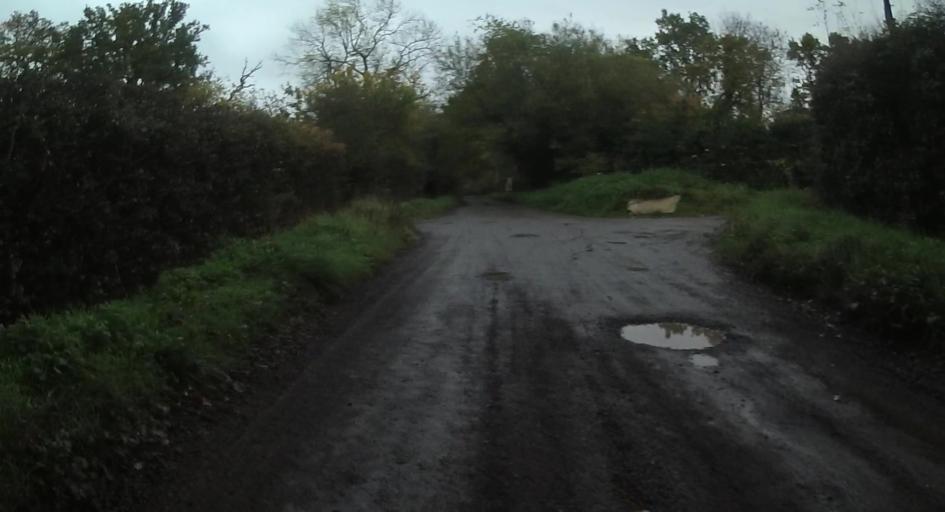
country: GB
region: England
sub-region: Surrey
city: Farnham
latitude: 51.2221
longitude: -0.8089
